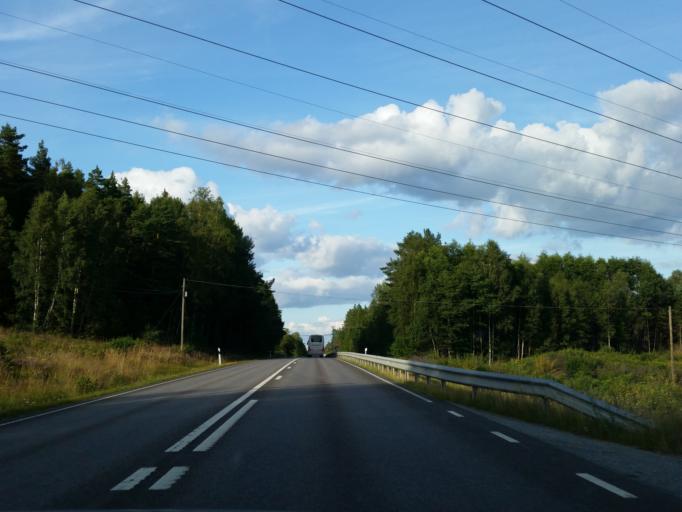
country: SE
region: Stockholm
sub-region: Sodertalje Kommun
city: Molnbo
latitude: 59.0654
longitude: 17.5224
